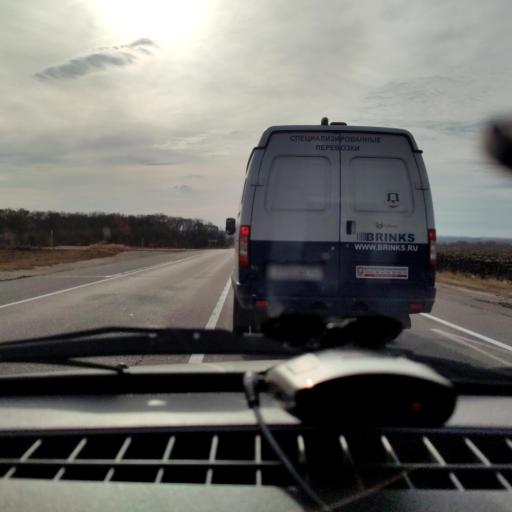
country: RU
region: Voronezj
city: Shilovo
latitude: 51.4593
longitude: 38.9708
